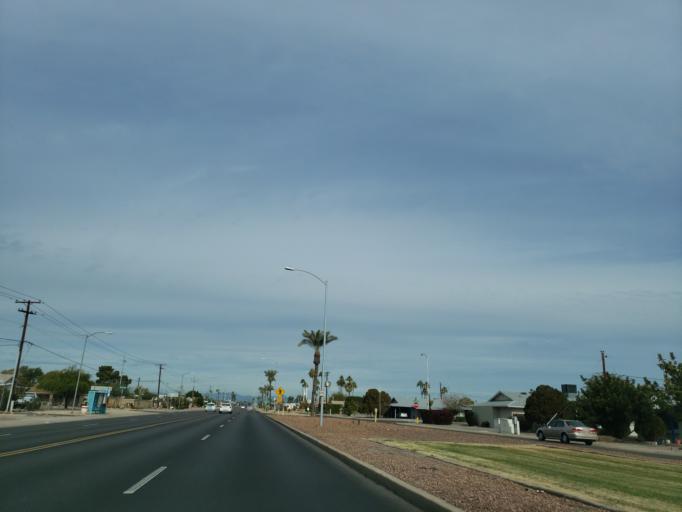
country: US
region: Arizona
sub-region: Maricopa County
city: Youngtown
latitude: 33.5881
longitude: -112.2987
